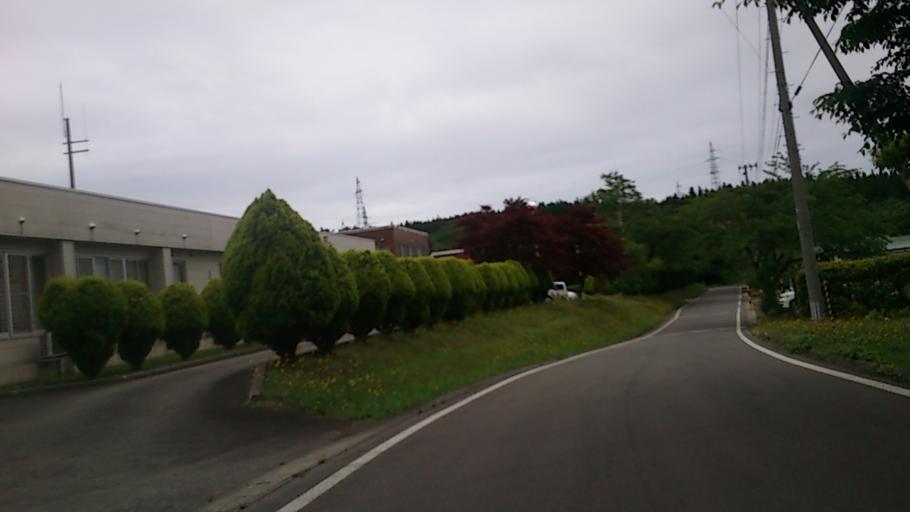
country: JP
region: Yamagata
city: Yuza
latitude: 39.1677
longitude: 139.9483
